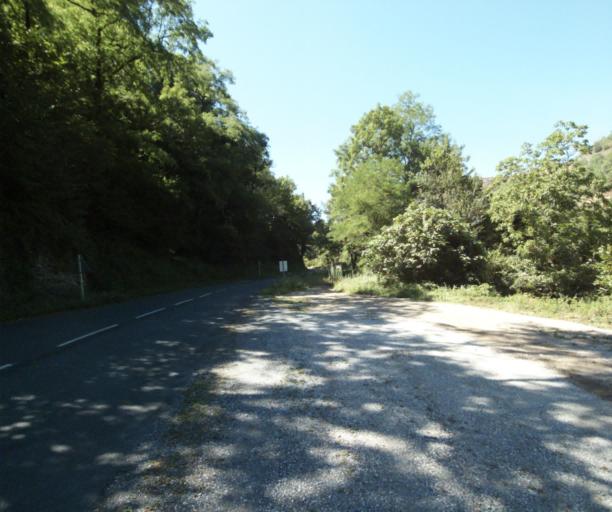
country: FR
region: Midi-Pyrenees
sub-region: Departement du Tarn
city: Soreze
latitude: 43.4405
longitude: 2.0872
